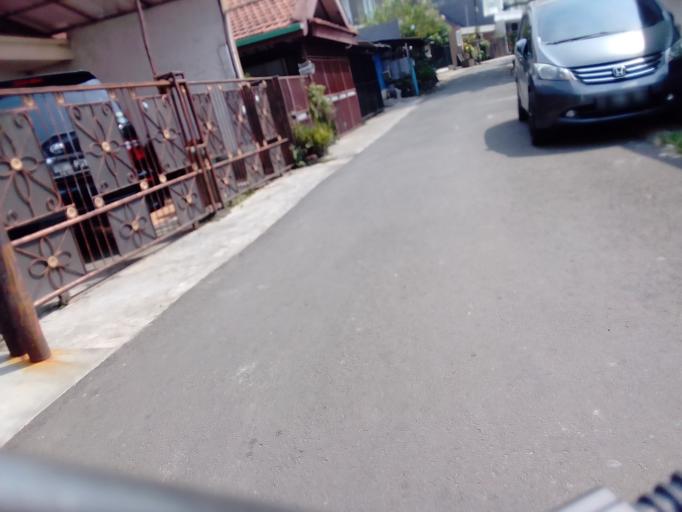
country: ID
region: Jakarta Raya
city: Jakarta
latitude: -6.2103
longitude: 106.8085
